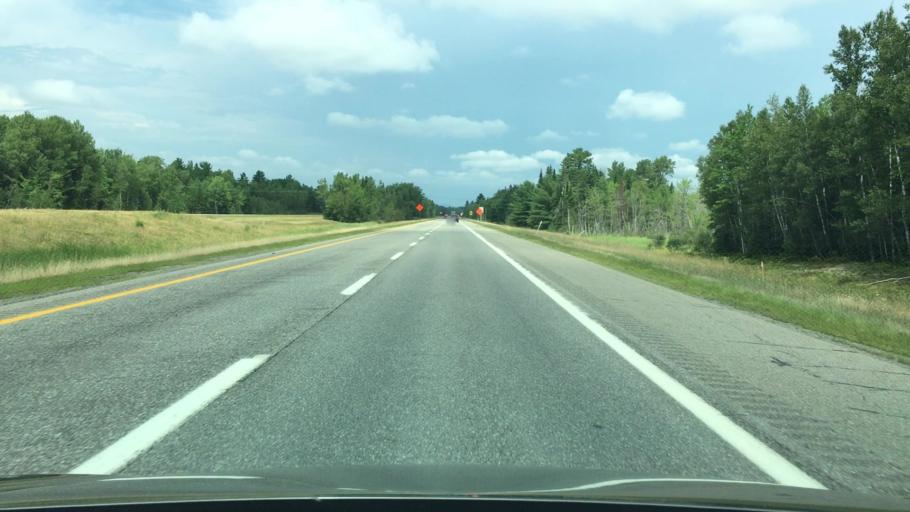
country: US
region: Maine
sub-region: Penobscot County
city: Howland
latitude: 45.2448
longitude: -68.6780
